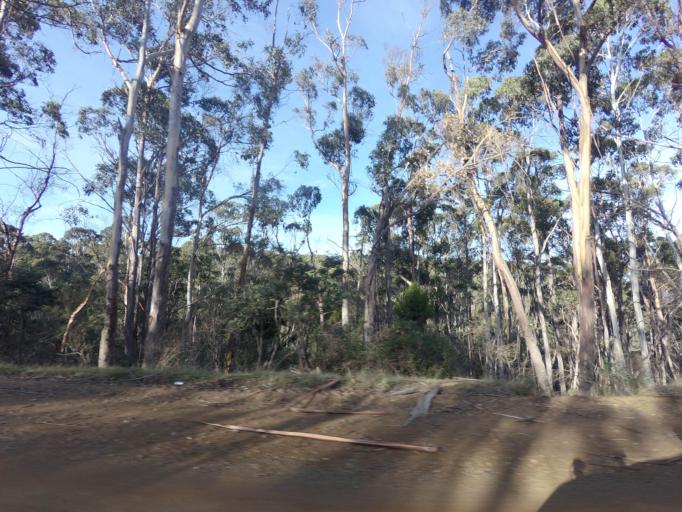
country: AU
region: Tasmania
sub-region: Brighton
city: Bridgewater
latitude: -42.4887
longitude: 147.3853
